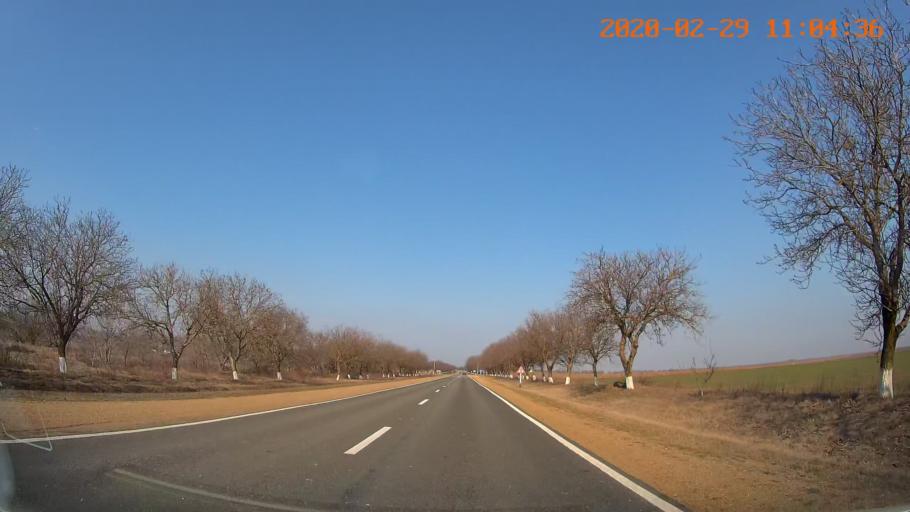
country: MD
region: Criuleni
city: Criuleni
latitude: 47.1914
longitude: 29.2003
